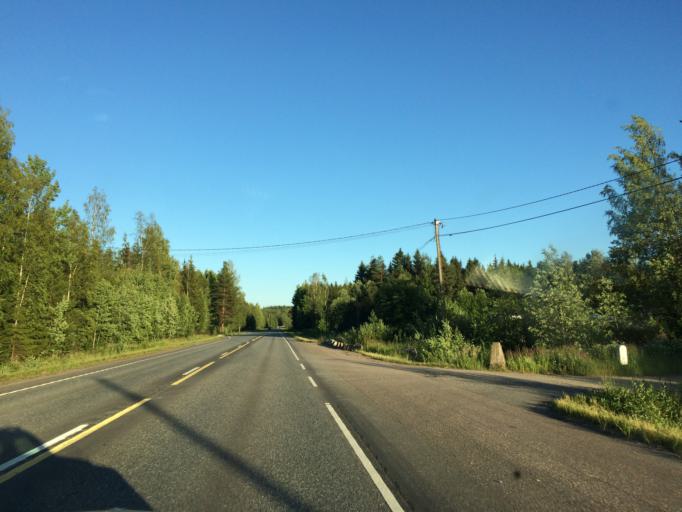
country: FI
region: Haeme
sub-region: Haemeenlinna
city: Tervakoski
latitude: 60.7760
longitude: 24.6966
